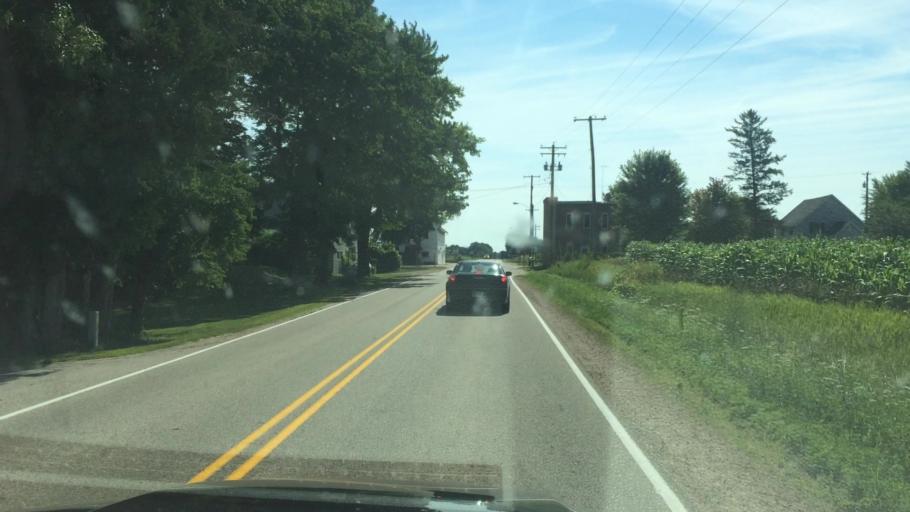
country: US
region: Wisconsin
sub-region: Oconto County
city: Gillett
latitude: 44.7874
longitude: -88.3341
